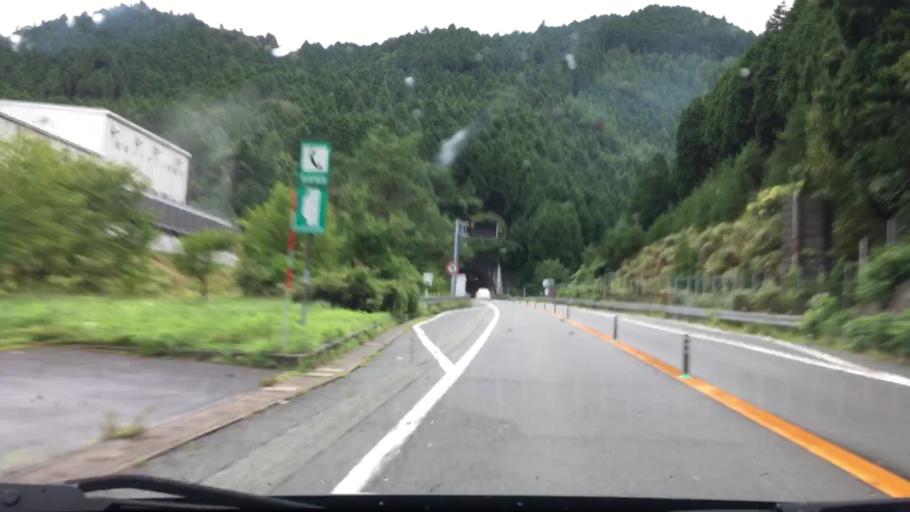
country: JP
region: Hyogo
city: Nishiwaki
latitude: 35.1468
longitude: 134.7881
